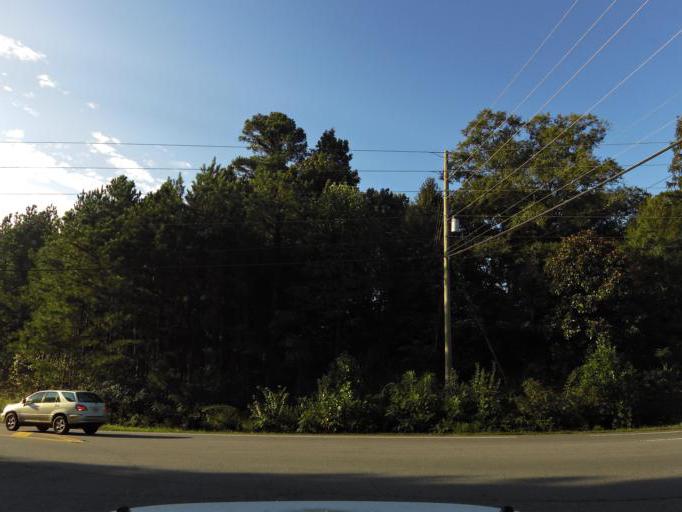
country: US
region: Georgia
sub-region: Cobb County
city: Kennesaw
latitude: 33.9648
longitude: -84.6173
